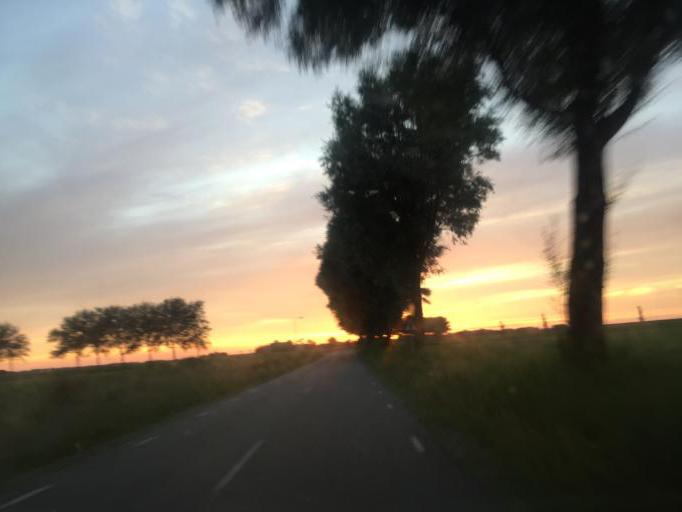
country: NL
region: Friesland
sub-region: Gemeente Dongeradeel
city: Anjum
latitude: 53.3893
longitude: 6.1051
